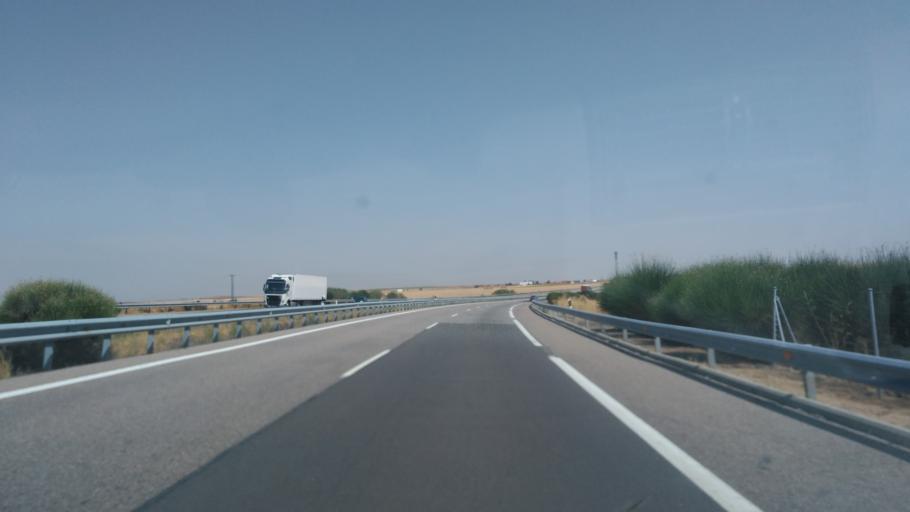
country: ES
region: Castille and Leon
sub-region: Provincia de Salamanca
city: Doninos de Salamanca
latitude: 40.9439
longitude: -5.7691
